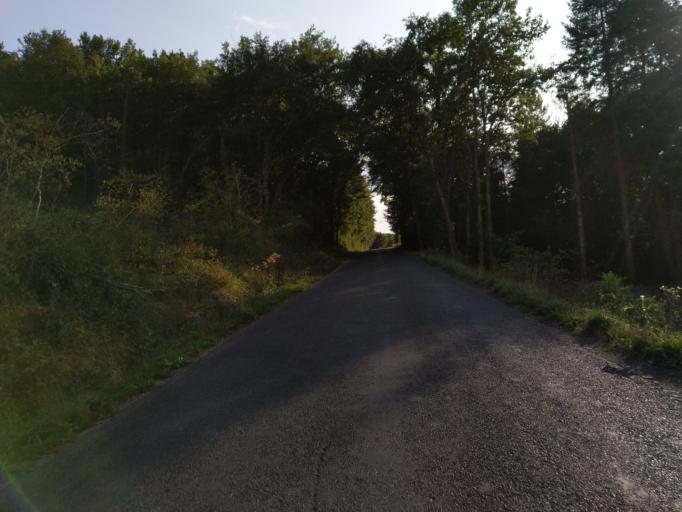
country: FR
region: Midi-Pyrenees
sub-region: Departement du Tarn
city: Frejairolles
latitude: 43.8454
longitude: 2.2272
